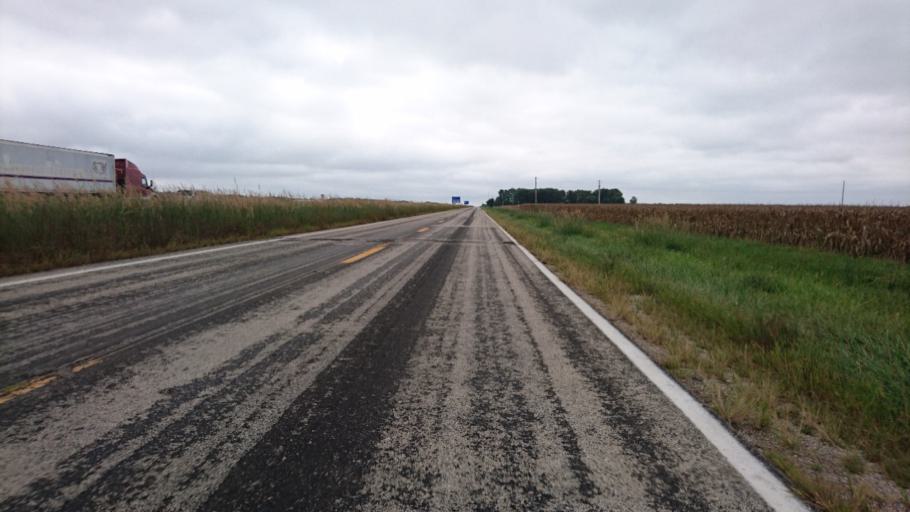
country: US
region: Illinois
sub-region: Montgomery County
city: Raymond
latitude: 39.3090
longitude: -89.6429
